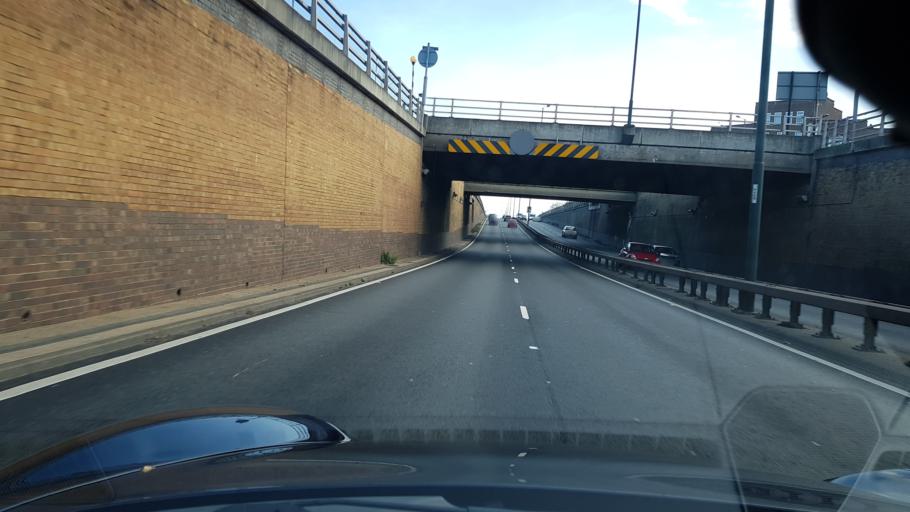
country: GB
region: England
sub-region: Greater London
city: Hook
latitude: 51.3754
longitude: -0.3048
